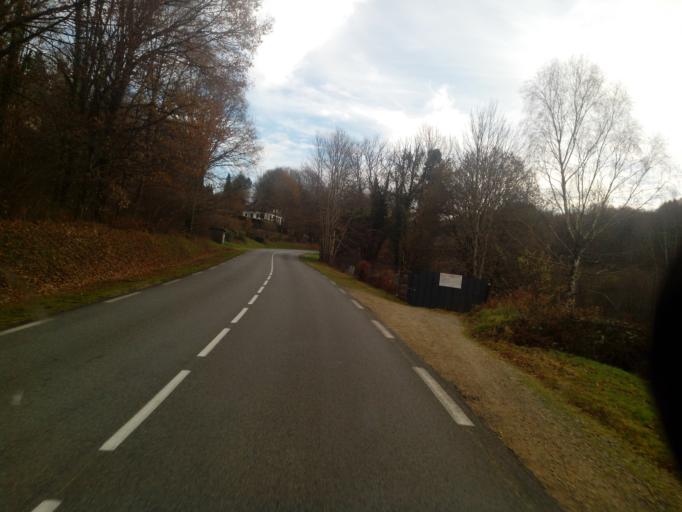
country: FR
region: Limousin
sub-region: Departement de la Haute-Vienne
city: Eymoutiers
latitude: 45.7323
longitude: 1.7490
